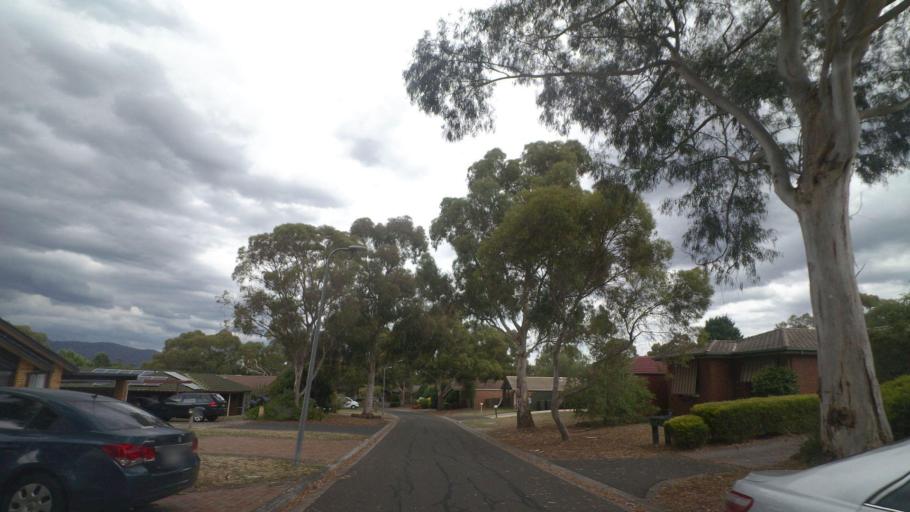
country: AU
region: Victoria
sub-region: Maroondah
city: Croydon South
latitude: -37.8183
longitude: 145.2825
